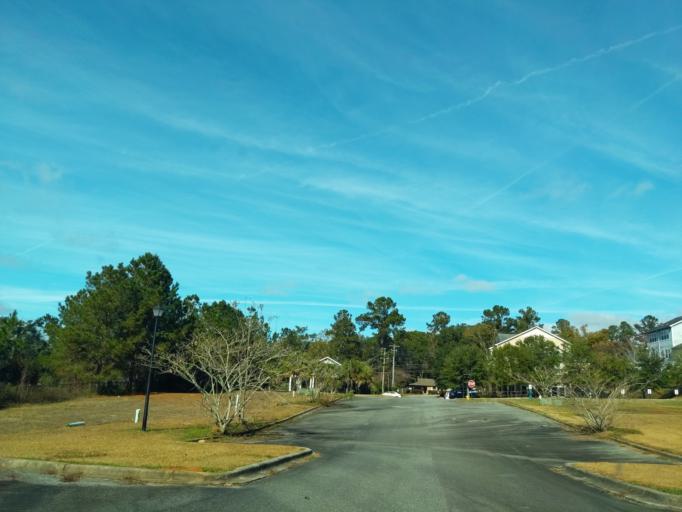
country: US
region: Florida
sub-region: Leon County
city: Tallahassee
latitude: 30.4724
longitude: -84.3437
